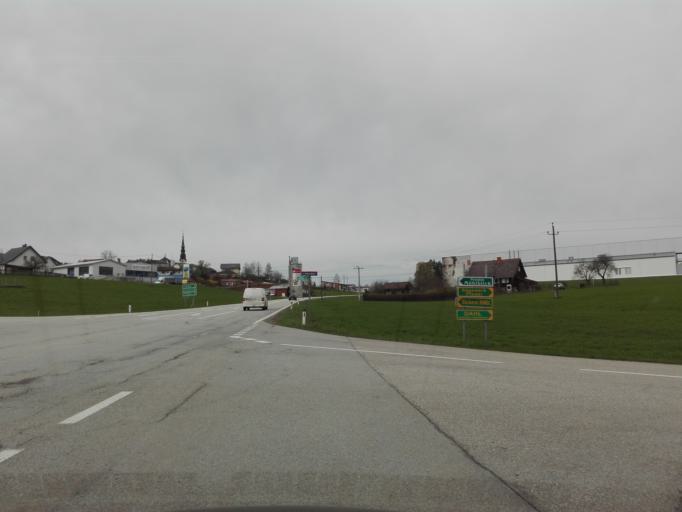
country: AT
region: Upper Austria
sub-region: Politischer Bezirk Rohrbach
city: Ulrichsberg
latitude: 48.6747
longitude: 13.9191
